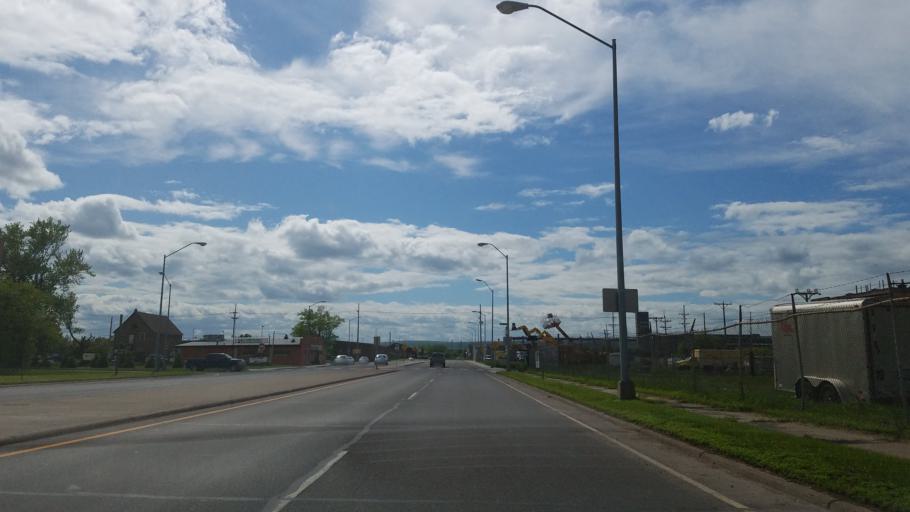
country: US
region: Wisconsin
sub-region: Douglas County
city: Superior
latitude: 46.7352
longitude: -92.0974
